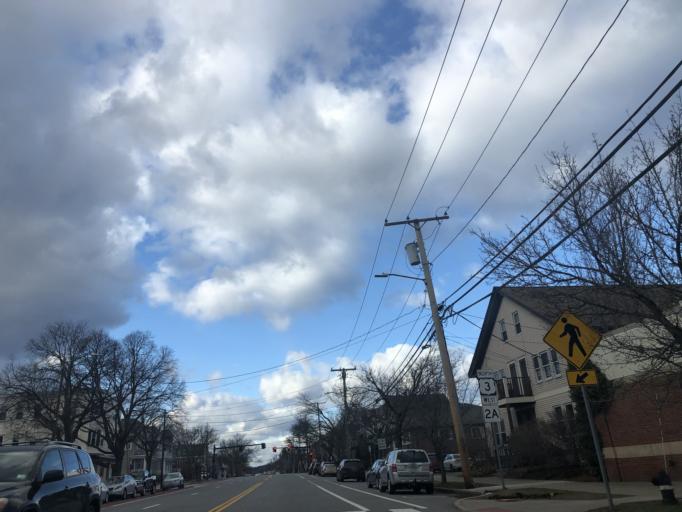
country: US
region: Massachusetts
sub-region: Middlesex County
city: Arlington
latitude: 42.4017
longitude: -71.1372
